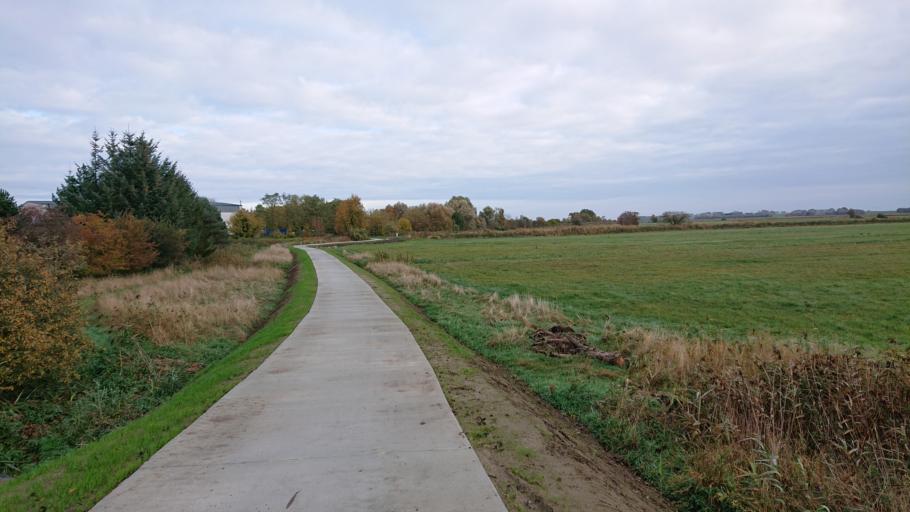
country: DE
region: Mecklenburg-Vorpommern
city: Barth
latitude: 54.3670
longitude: 12.7403
